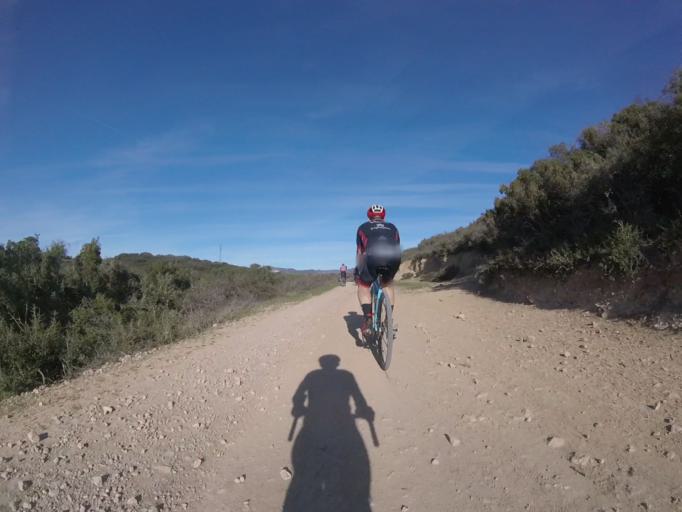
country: ES
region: Navarre
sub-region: Provincia de Navarra
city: Yerri
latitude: 42.6990
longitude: -1.9647
